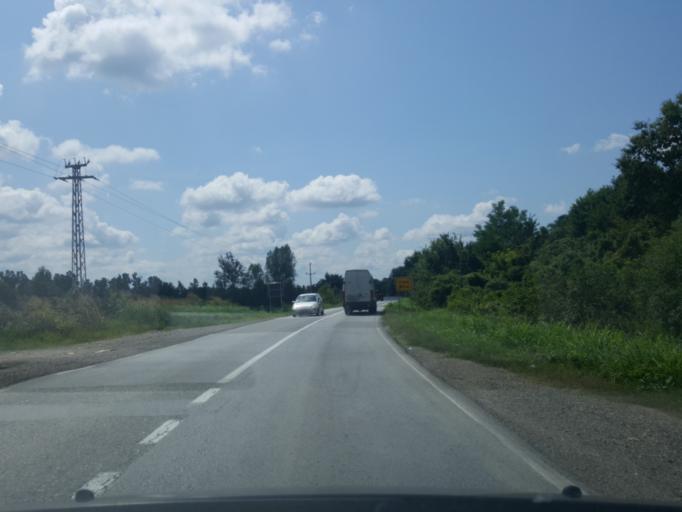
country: RS
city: Glusci
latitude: 44.9236
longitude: 19.5443
